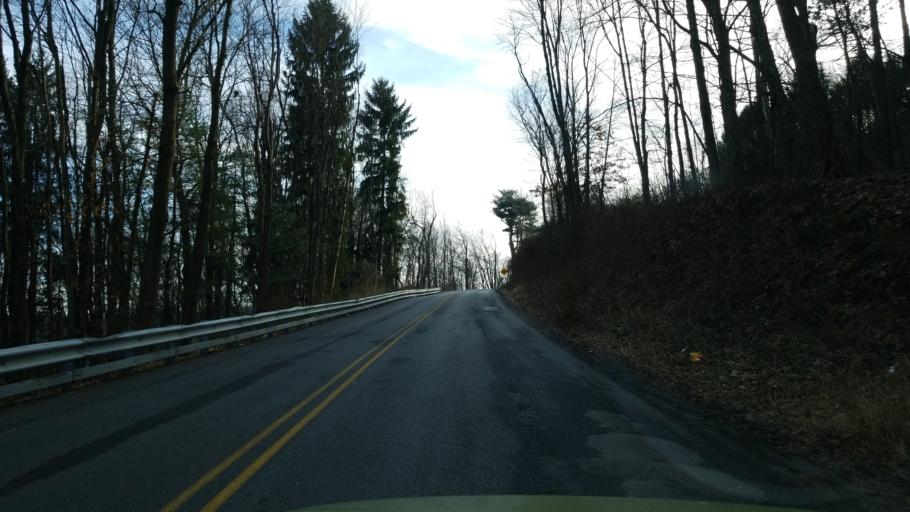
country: US
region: Pennsylvania
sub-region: Clearfield County
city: Clearfield
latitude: 41.0184
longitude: -78.4462
